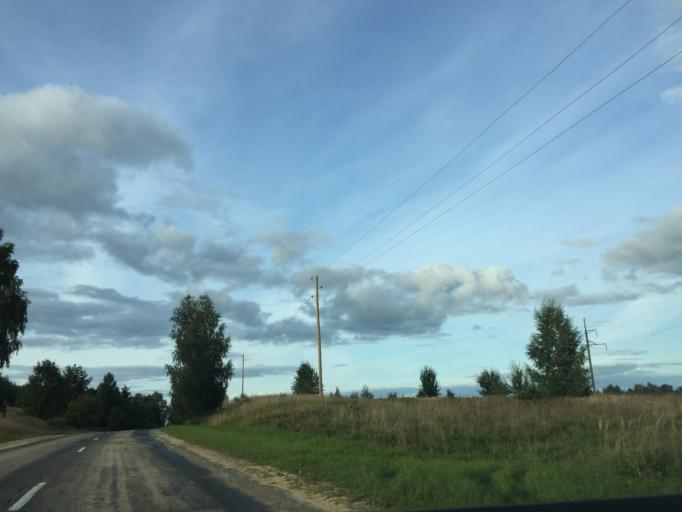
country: LV
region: Nereta
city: Nereta
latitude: 56.2467
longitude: 25.3322
